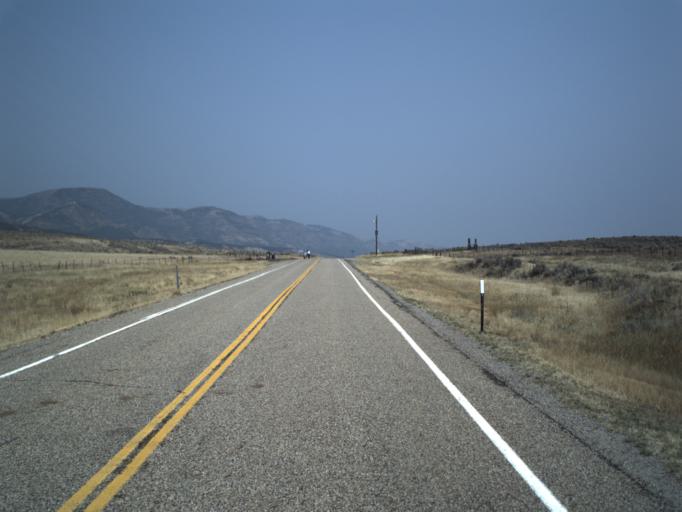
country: US
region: Utah
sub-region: Morgan County
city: Morgan
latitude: 40.9519
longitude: -111.5496
